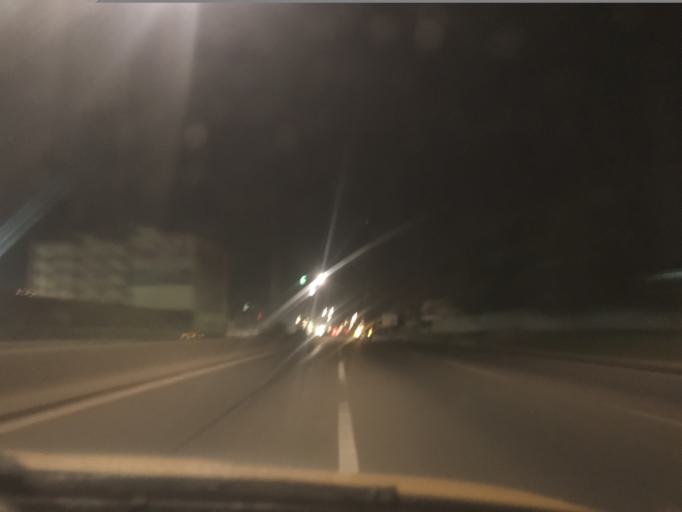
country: SN
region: Dakar
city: Grand Dakar
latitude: 14.7188
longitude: -17.4408
